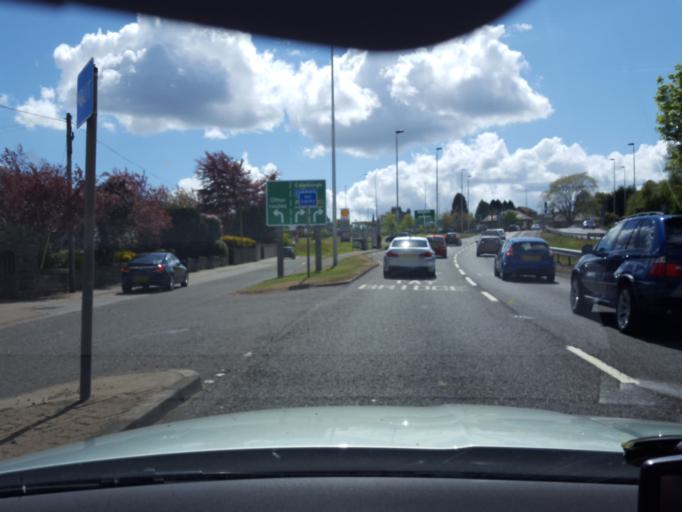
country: GB
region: Scotland
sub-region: Dundee City
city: Dundee
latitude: 56.4817
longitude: -2.9519
